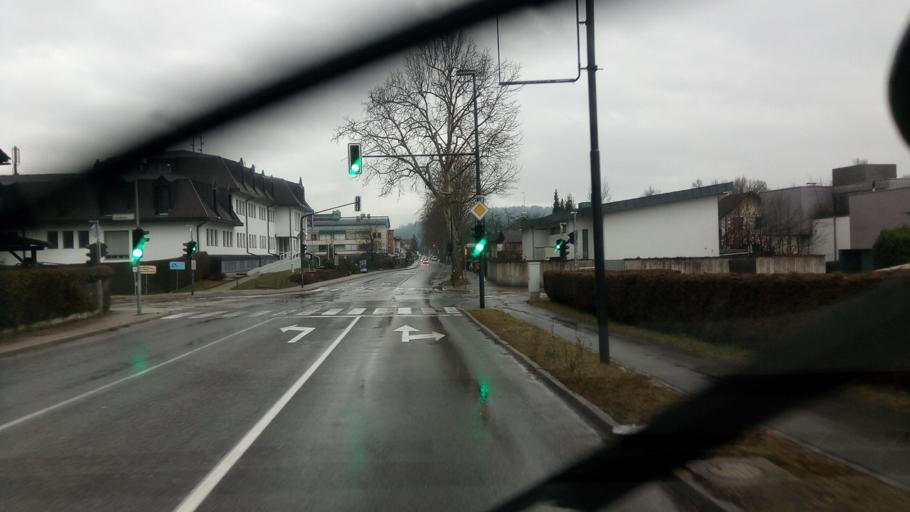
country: SI
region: Ljubljana
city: Ljubljana
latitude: 46.0727
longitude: 14.4661
